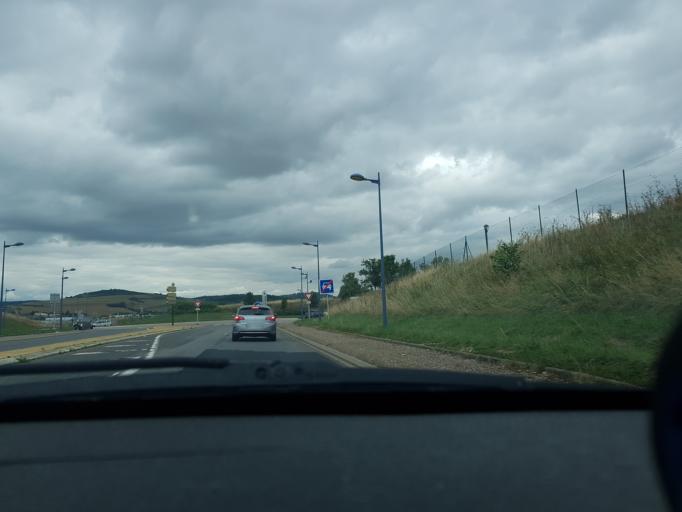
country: FR
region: Lorraine
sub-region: Departement de Meurthe-et-Moselle
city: Saulxures-les-Nancy
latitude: 48.6975
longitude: 6.2429
